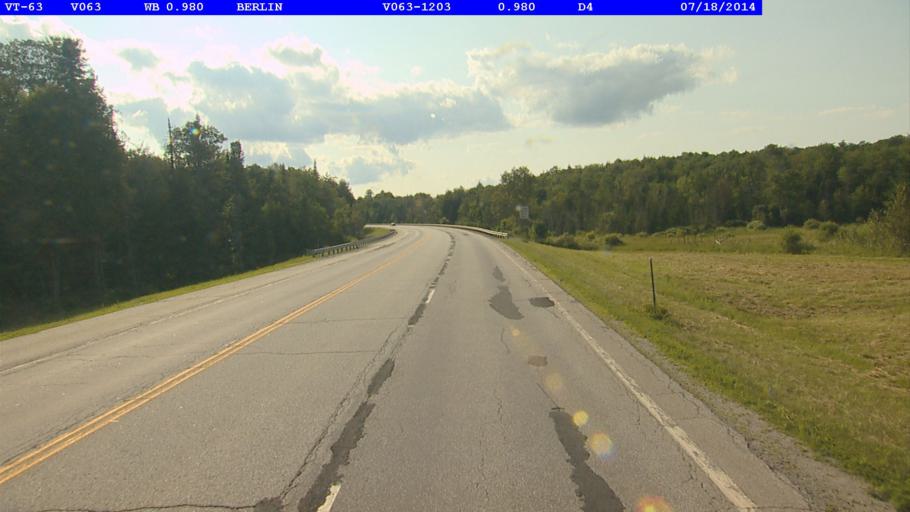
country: US
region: Vermont
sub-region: Orange County
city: Williamstown
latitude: 44.1662
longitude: -72.5583
